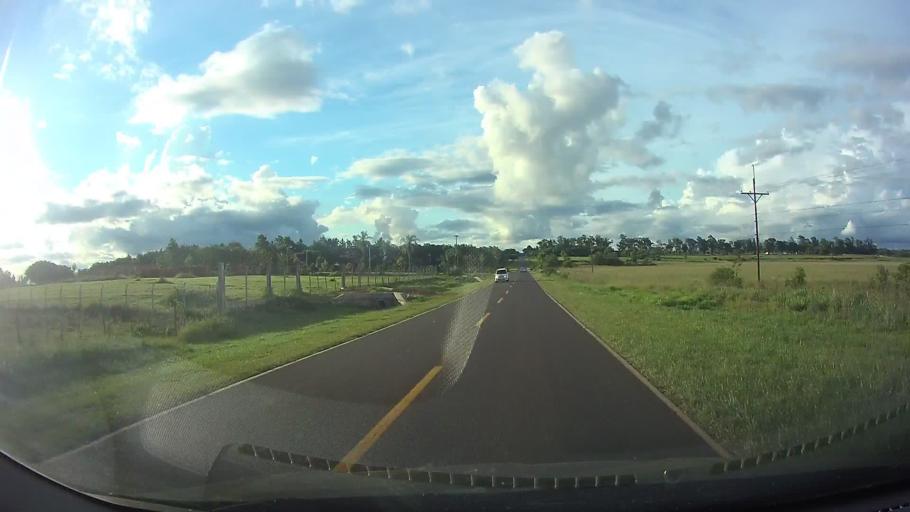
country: PY
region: Paraguari
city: Ybycui
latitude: -25.9997
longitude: -57.0471
